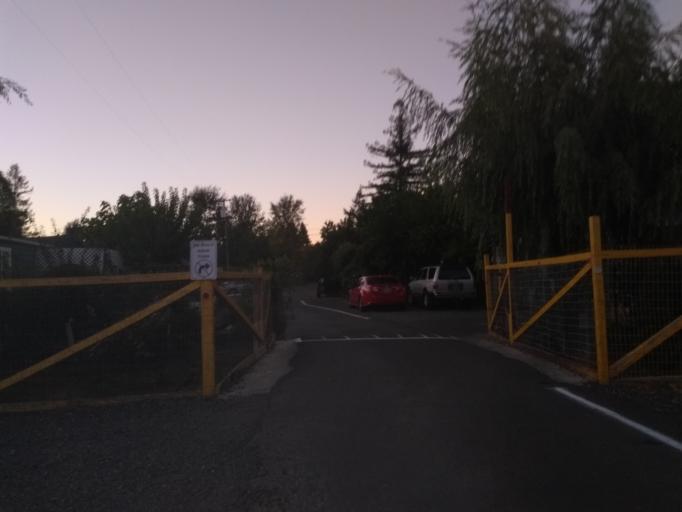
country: US
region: California
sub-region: Mendocino County
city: Ukiah
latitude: 39.1389
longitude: -123.2079
